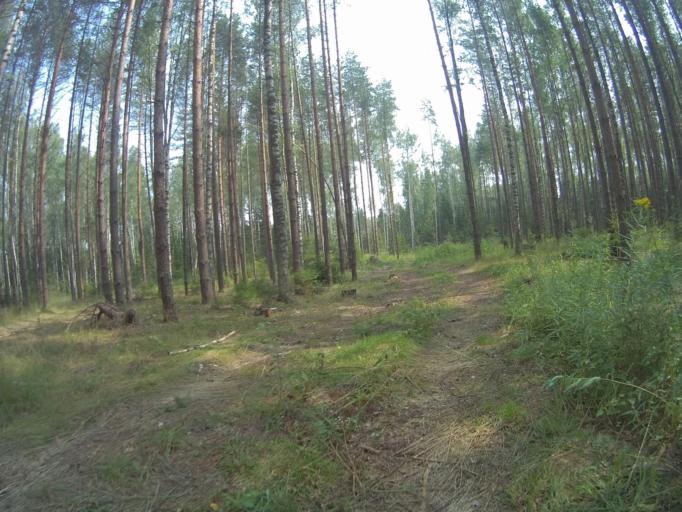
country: RU
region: Vladimir
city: Vorsha
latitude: 55.9657
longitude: 40.1933
